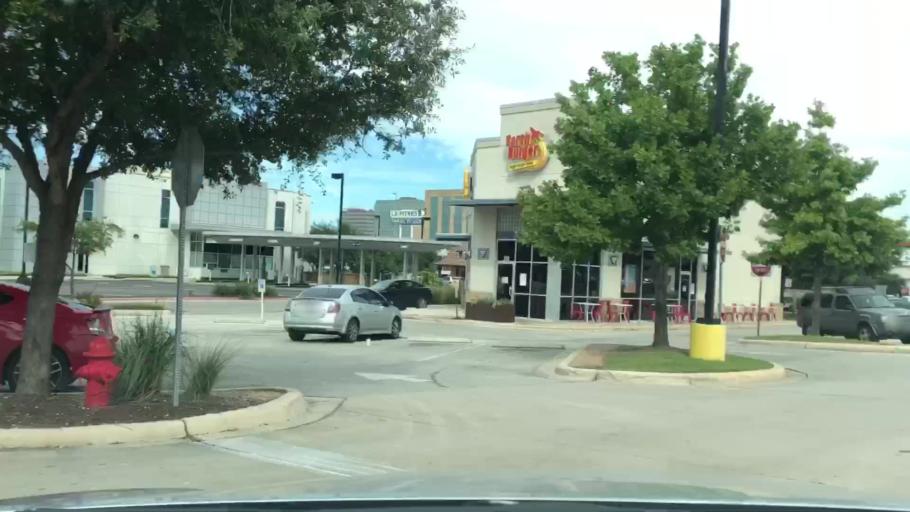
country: US
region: Texas
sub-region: Bexar County
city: Castle Hills
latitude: 29.5191
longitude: -98.5056
